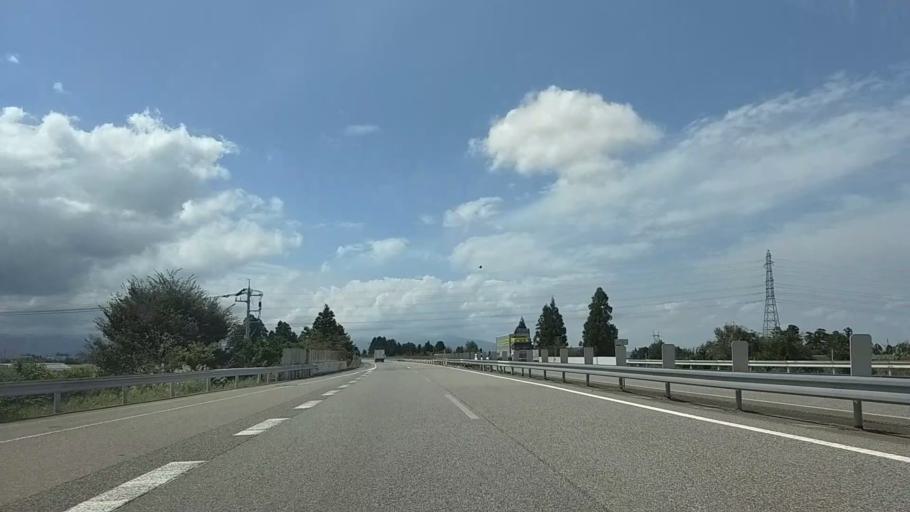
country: JP
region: Toyama
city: Toyama-shi
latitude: 36.6634
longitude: 137.2667
